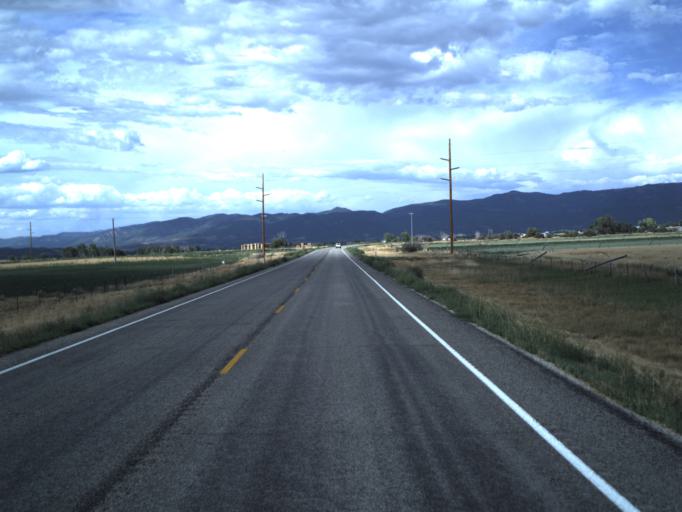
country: US
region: Utah
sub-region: Sanpete County
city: Mount Pleasant
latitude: 39.5085
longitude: -111.4975
